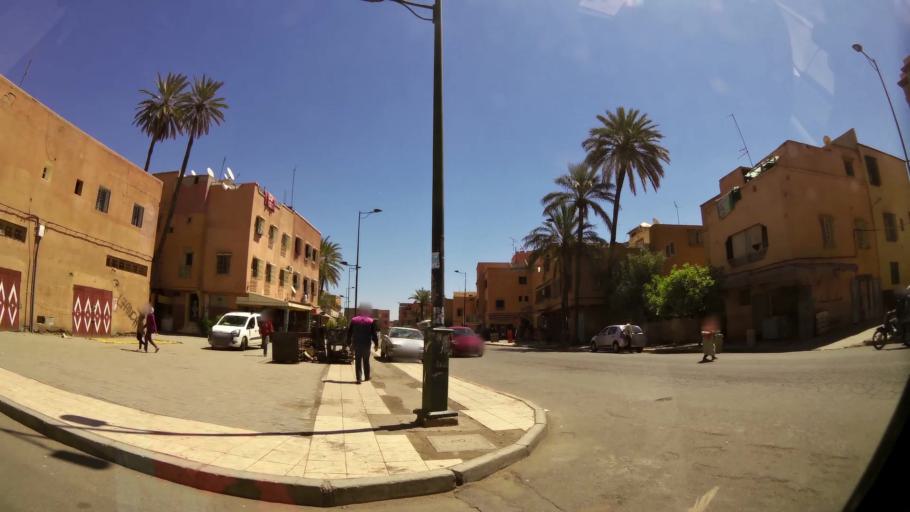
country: MA
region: Marrakech-Tensift-Al Haouz
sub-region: Marrakech
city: Marrakesh
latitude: 31.6536
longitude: -7.9915
